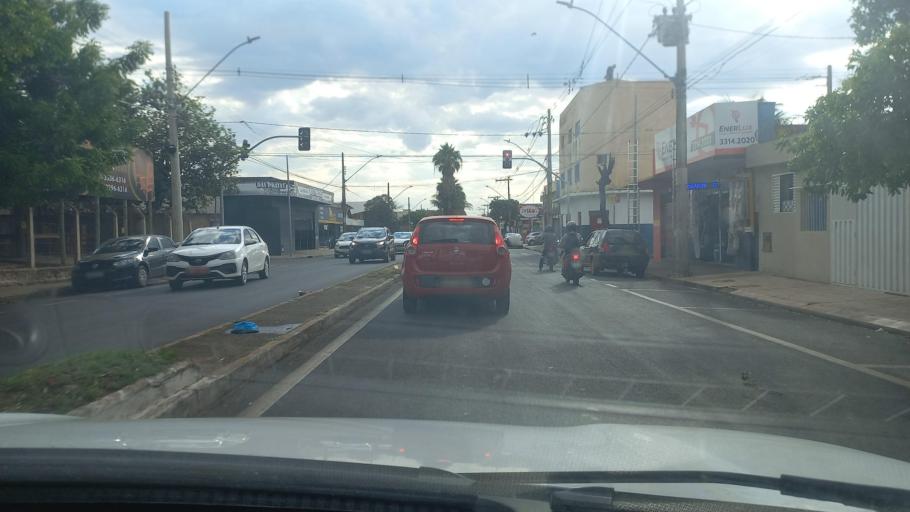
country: BR
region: Minas Gerais
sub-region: Uberaba
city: Uberaba
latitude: -19.7685
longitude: -47.9252
